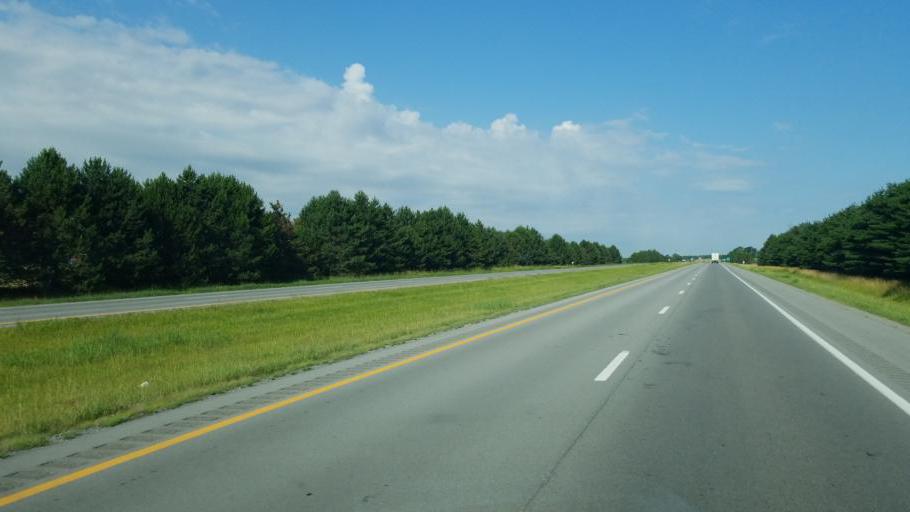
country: US
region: Ohio
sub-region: Hancock County
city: Findlay
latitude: 40.9864
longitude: -83.6208
